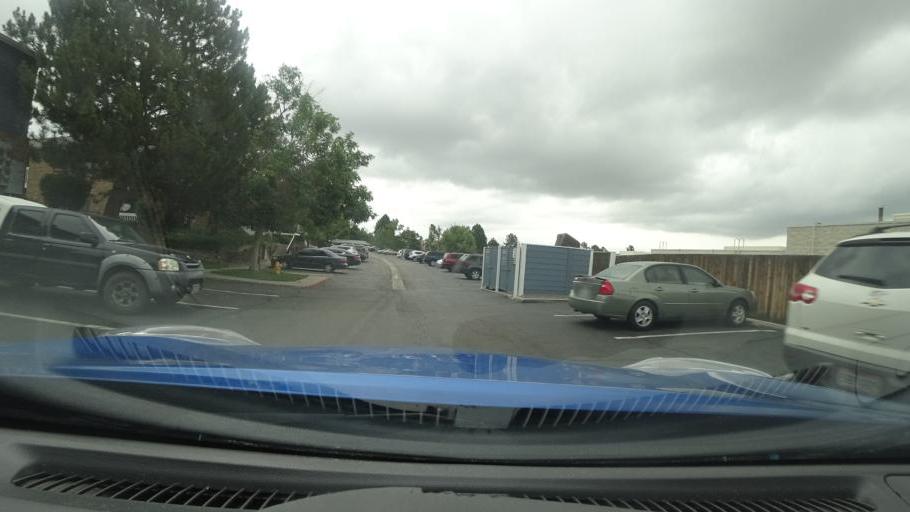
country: US
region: Colorado
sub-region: Adams County
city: Aurora
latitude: 39.6971
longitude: -104.8136
